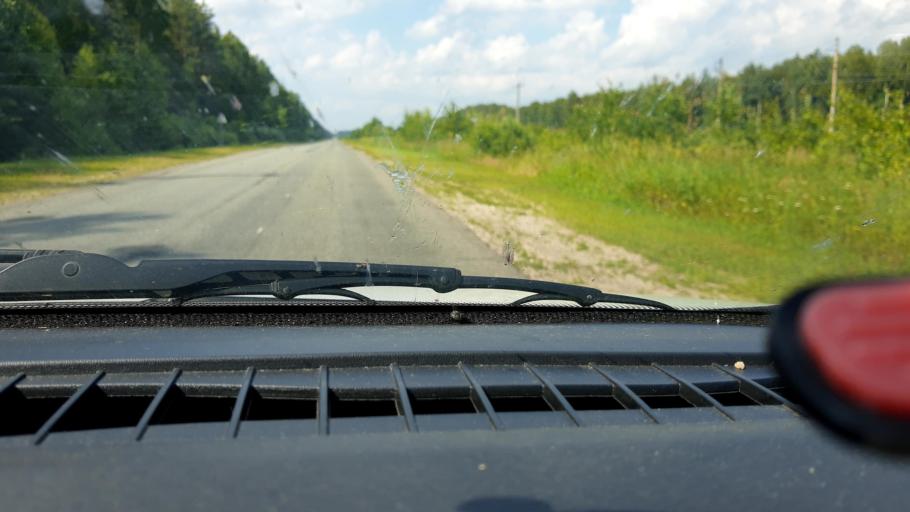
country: RU
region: Nizjnij Novgorod
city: Prudy
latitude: 57.4484
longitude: 46.0526
